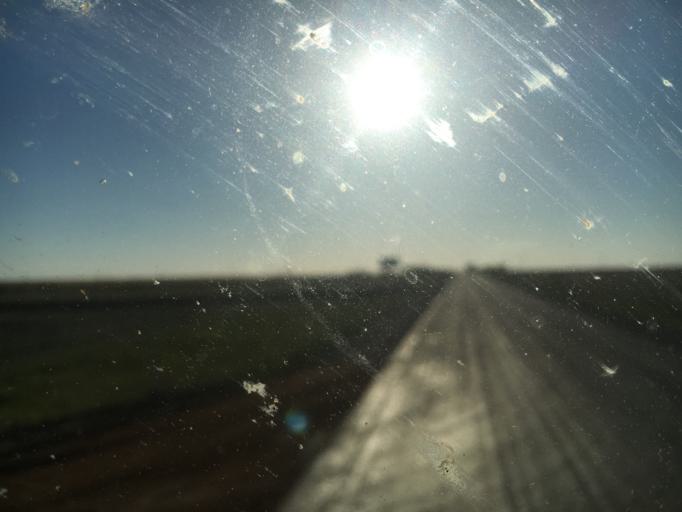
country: KZ
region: Aqtoebe
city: Batamshinskiy
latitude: 50.2485
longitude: 57.9879
